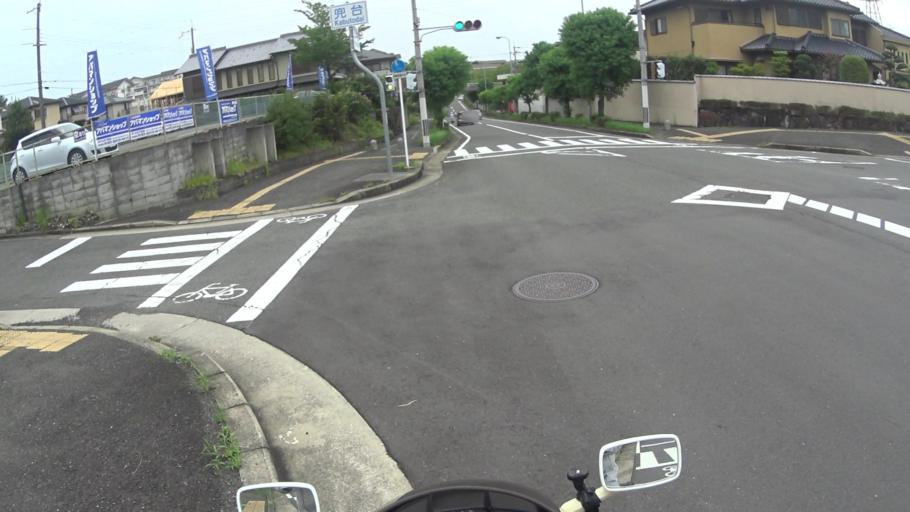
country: JP
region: Nara
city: Nara-shi
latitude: 34.7272
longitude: 135.7847
